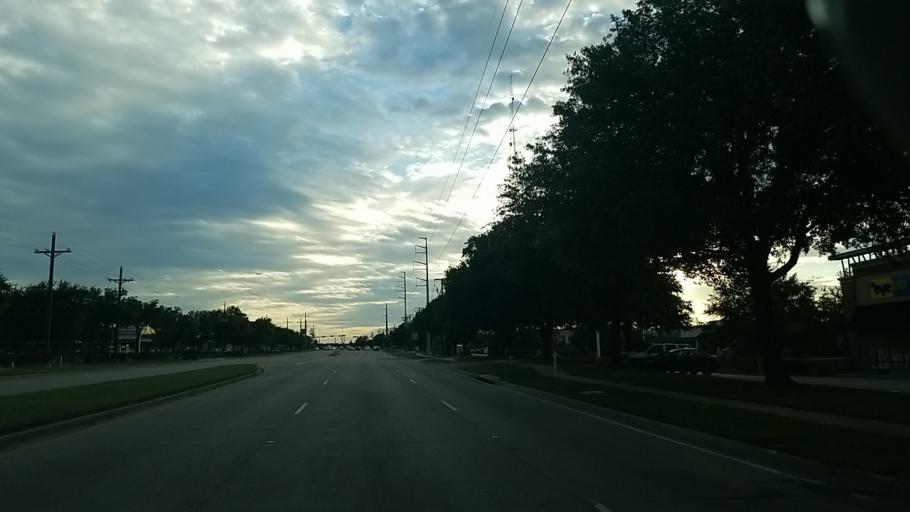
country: US
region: Texas
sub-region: Denton County
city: Lewisville
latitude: 33.0048
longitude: -96.9792
